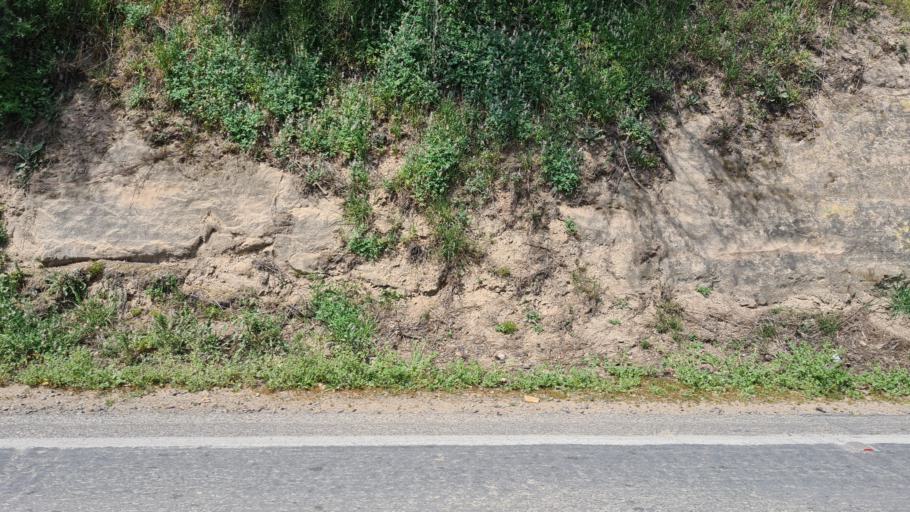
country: CL
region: O'Higgins
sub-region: Provincia de Cachapoal
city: San Vicente
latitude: -34.1561
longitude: -71.4237
